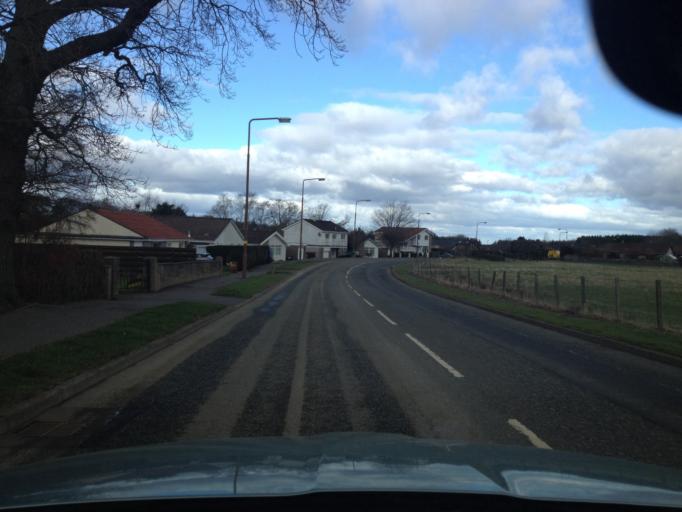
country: GB
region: Scotland
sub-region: West Lothian
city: Mid Calder
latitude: 55.8662
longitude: -3.5027
